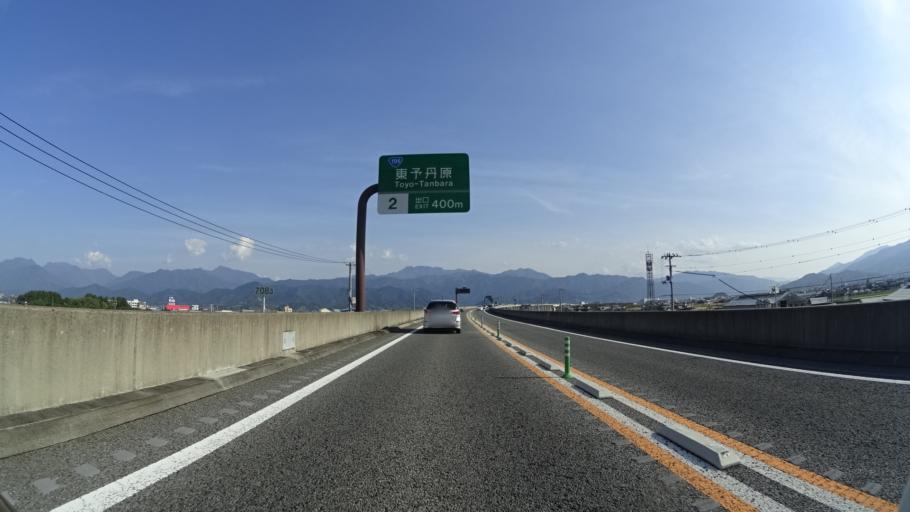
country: JP
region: Ehime
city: Saijo
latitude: 33.9251
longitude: 133.0744
